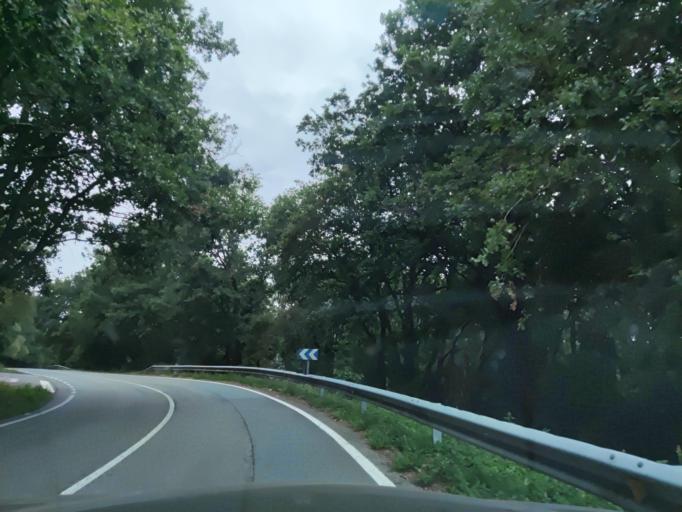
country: ES
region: Galicia
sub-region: Provincia da Coruna
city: Teo
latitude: 42.7642
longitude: -8.5557
